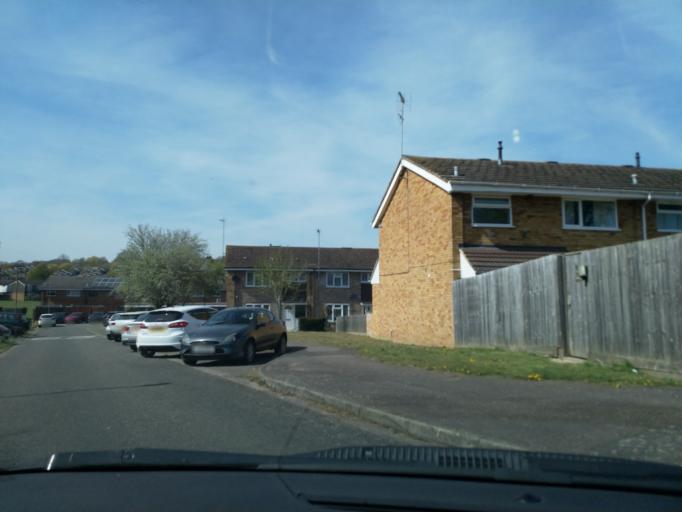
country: GB
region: England
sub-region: Oxfordshire
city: Banbury
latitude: 52.0693
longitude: -1.3497
